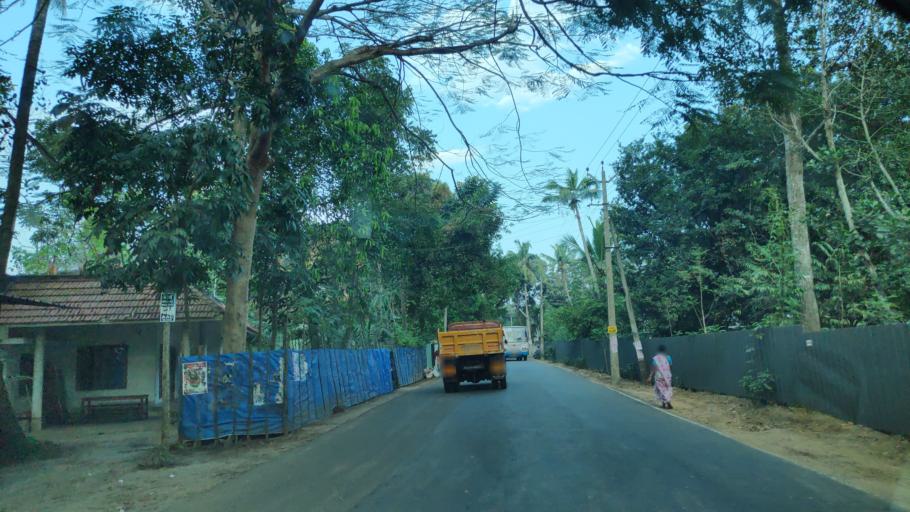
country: IN
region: Kerala
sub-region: Alappuzha
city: Shertallai
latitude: 9.6615
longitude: 76.3798
